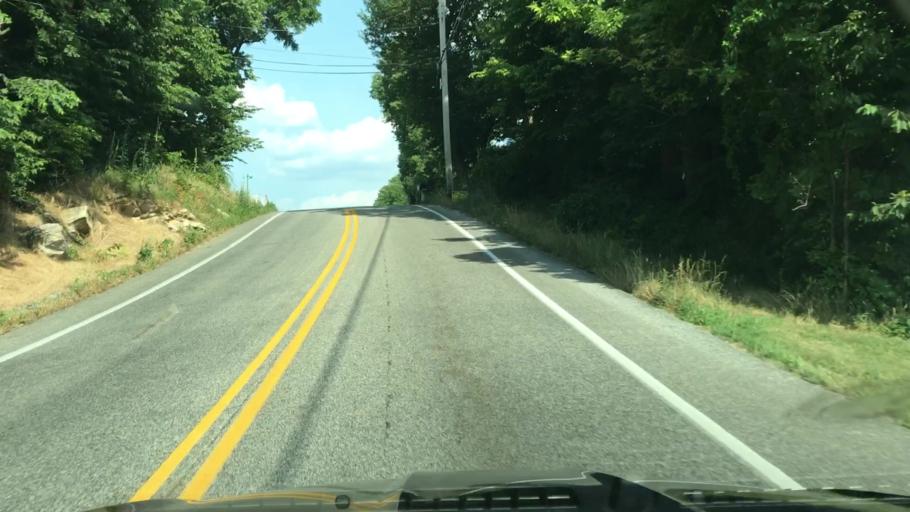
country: US
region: Pennsylvania
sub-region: Cumberland County
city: Mechanicsburg
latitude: 40.1734
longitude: -77.0620
